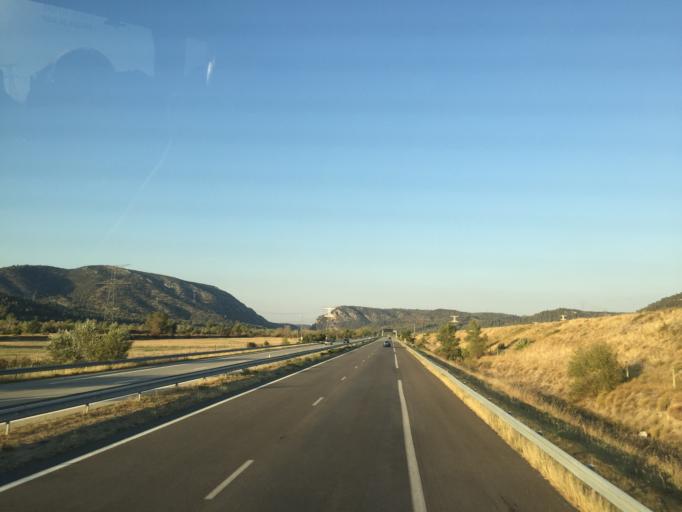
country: FR
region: Provence-Alpes-Cote d'Azur
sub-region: Departement des Bouches-du-Rhone
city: Jouques
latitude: 43.6598
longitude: 5.6222
